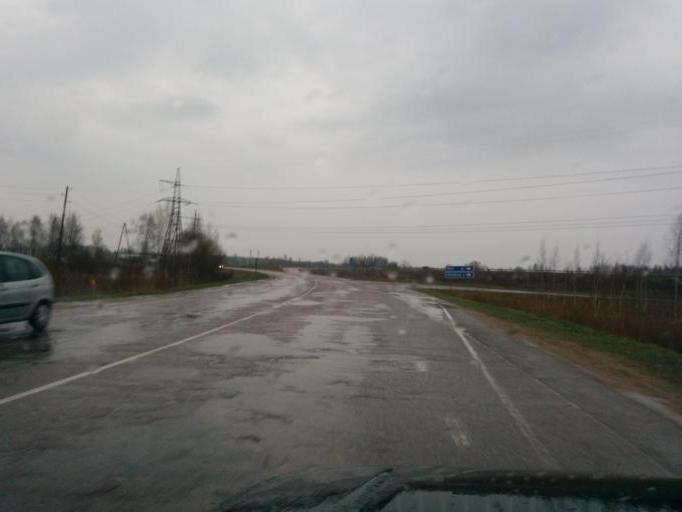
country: LV
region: Ozolnieku
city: Ozolnieki
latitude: 56.6555
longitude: 23.8000
